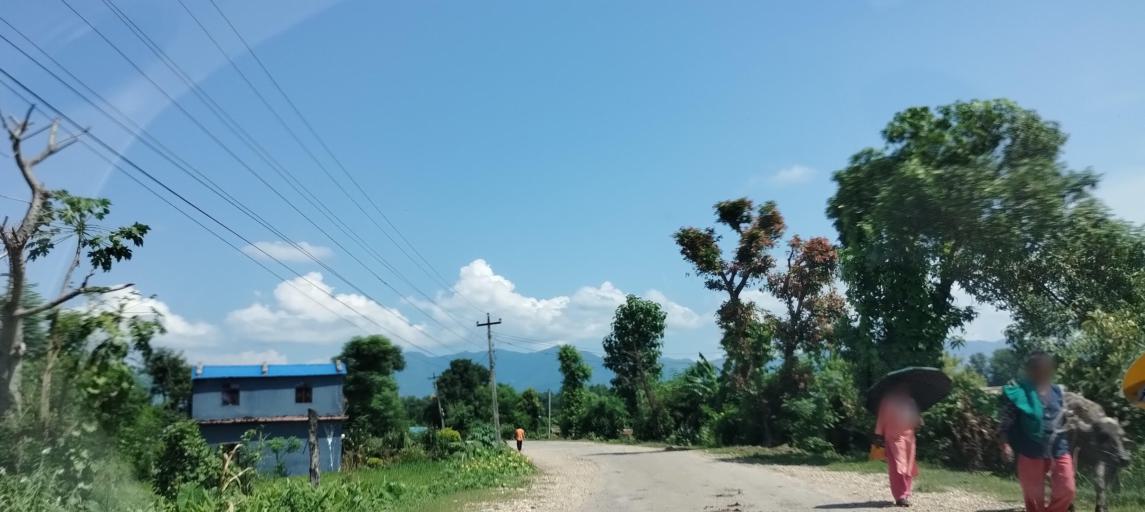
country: NP
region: Far Western
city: Tikapur
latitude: 28.5096
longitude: 81.3049
